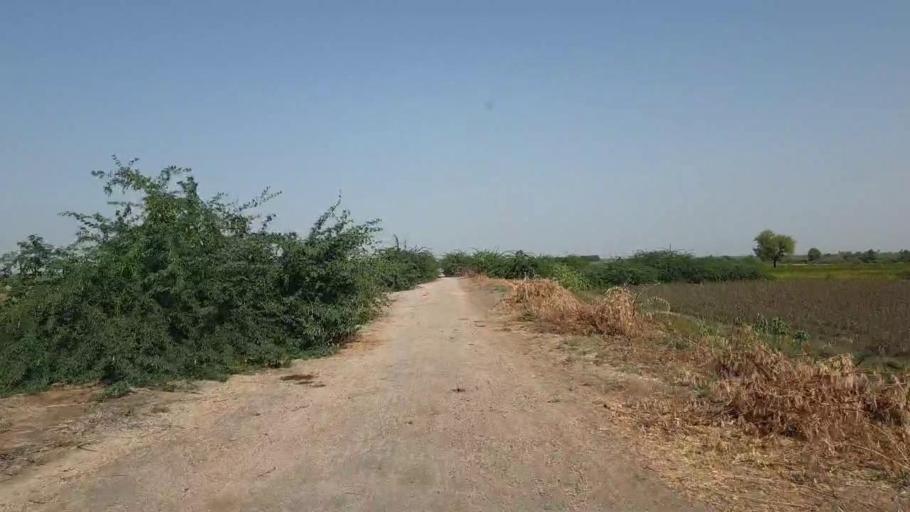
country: PK
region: Sindh
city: Tando Bago
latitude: 24.7108
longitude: 69.0720
